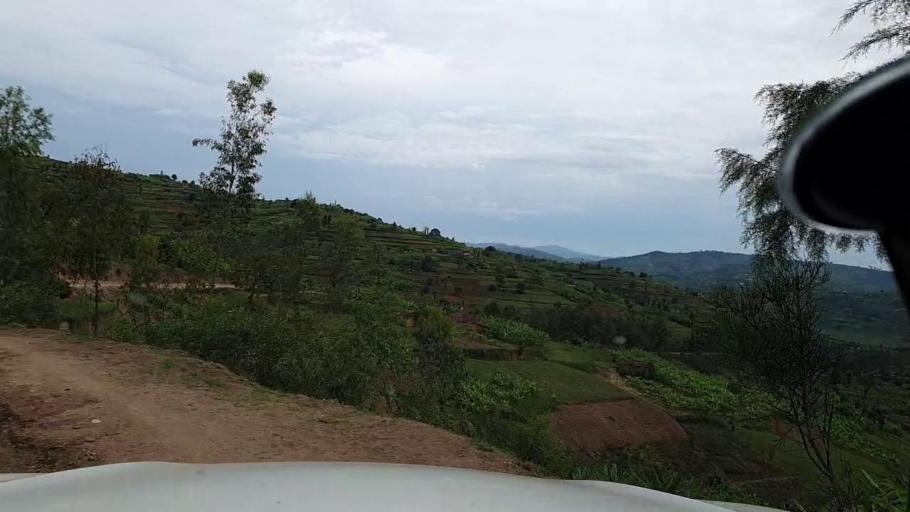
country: RW
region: Southern Province
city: Gitarama
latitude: -2.1332
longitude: 29.6610
